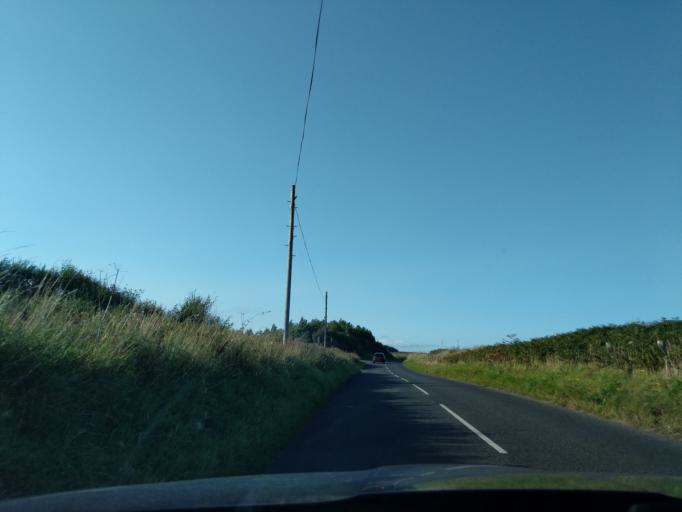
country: GB
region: England
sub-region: Northumberland
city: Lynemouth
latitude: 55.2123
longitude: -1.5285
